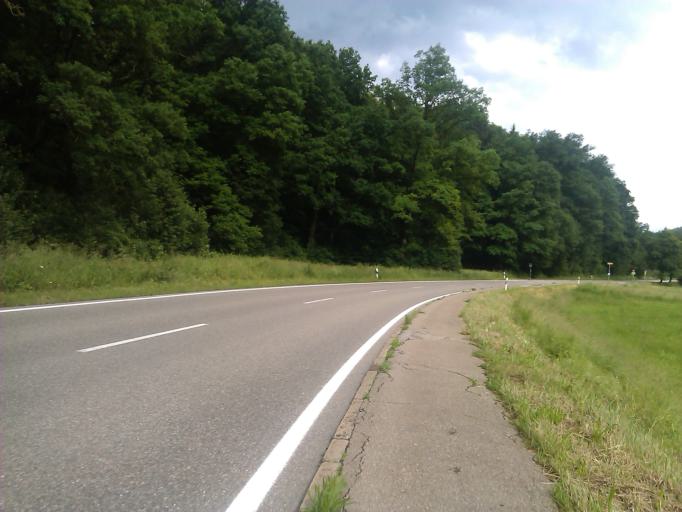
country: DE
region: Baden-Wuerttemberg
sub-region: Regierungsbezirk Stuttgart
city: Obergroningen
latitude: 48.9119
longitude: 9.9271
